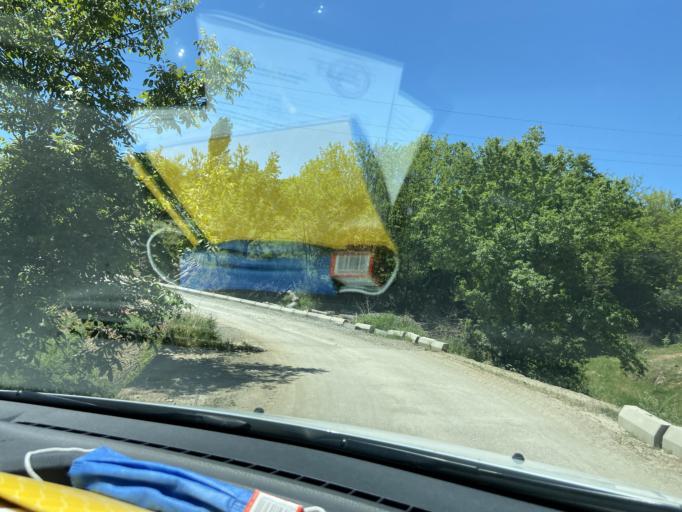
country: MK
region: Makedonska Kamenica
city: Makedonska Kamenica
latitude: 42.0167
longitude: 22.5707
